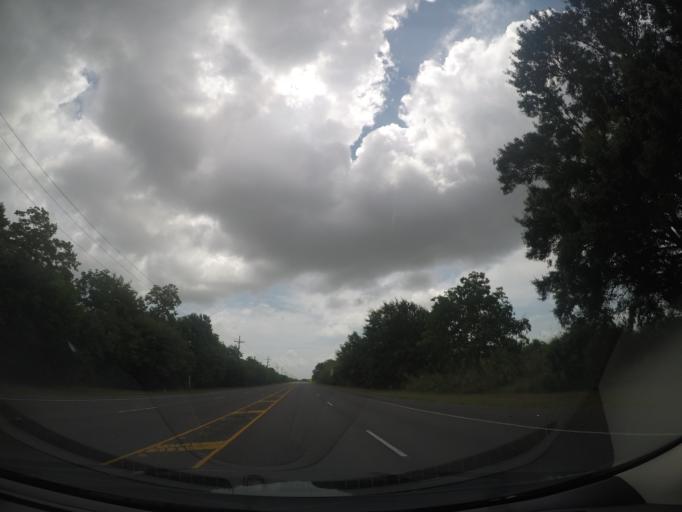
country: US
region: Louisiana
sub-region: Saint Tammany Parish
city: Eden Isle
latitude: 30.0674
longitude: -89.8323
